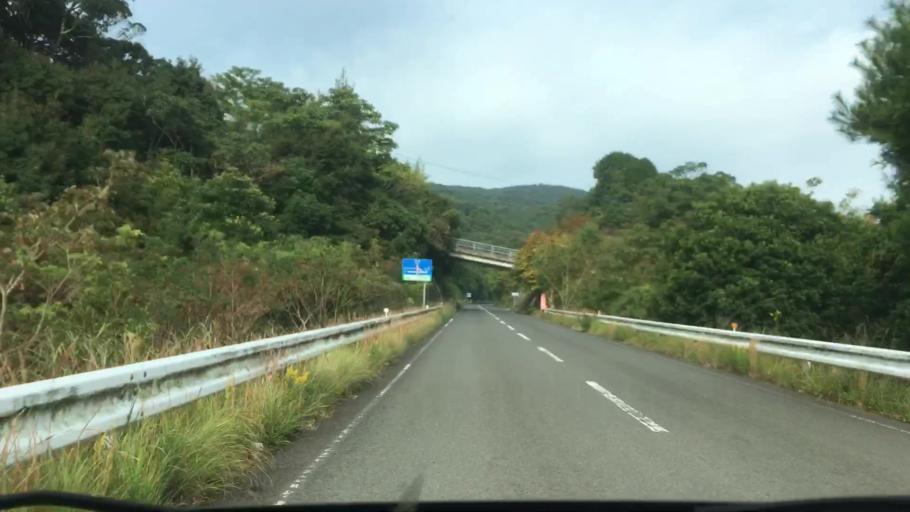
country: JP
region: Nagasaki
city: Sasebo
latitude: 32.9963
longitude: 129.7118
